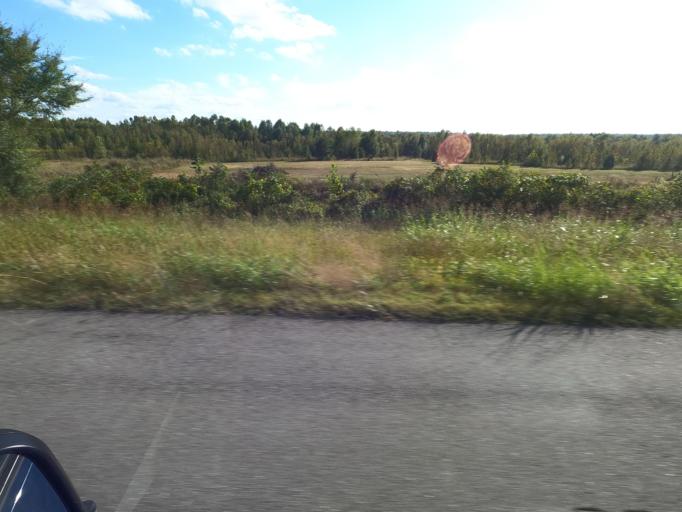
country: US
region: Tennessee
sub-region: Madison County
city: Jackson
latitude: 35.6688
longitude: -88.9237
